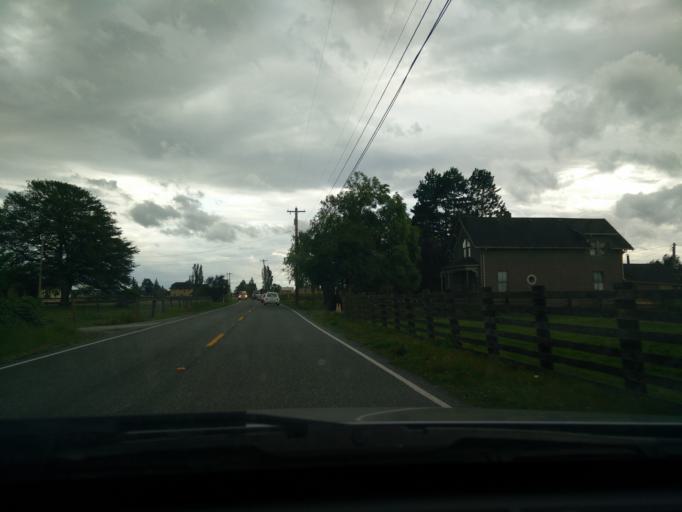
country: US
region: Washington
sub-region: Snohomish County
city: Stanwood
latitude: 48.2511
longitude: -122.3710
